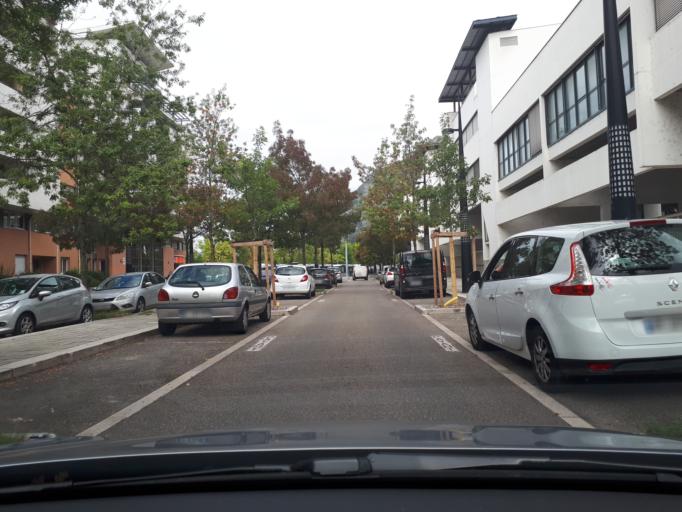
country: FR
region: Rhone-Alpes
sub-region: Departement de l'Isere
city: Saint-Martin-le-Vinoux
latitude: 45.1939
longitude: 5.7117
